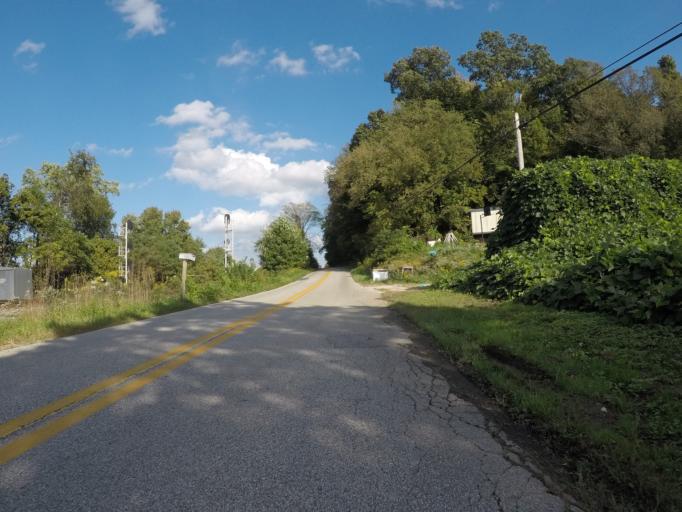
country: US
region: Ohio
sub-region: Lawrence County
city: Burlington
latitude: 38.3967
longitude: -82.5150
